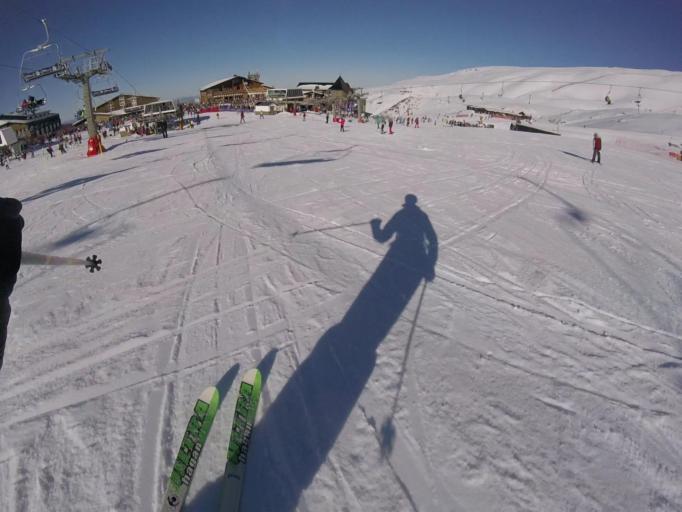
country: ES
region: Andalusia
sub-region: Provincia de Granada
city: Guejar-Sierra
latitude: 37.0702
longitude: -3.3882
